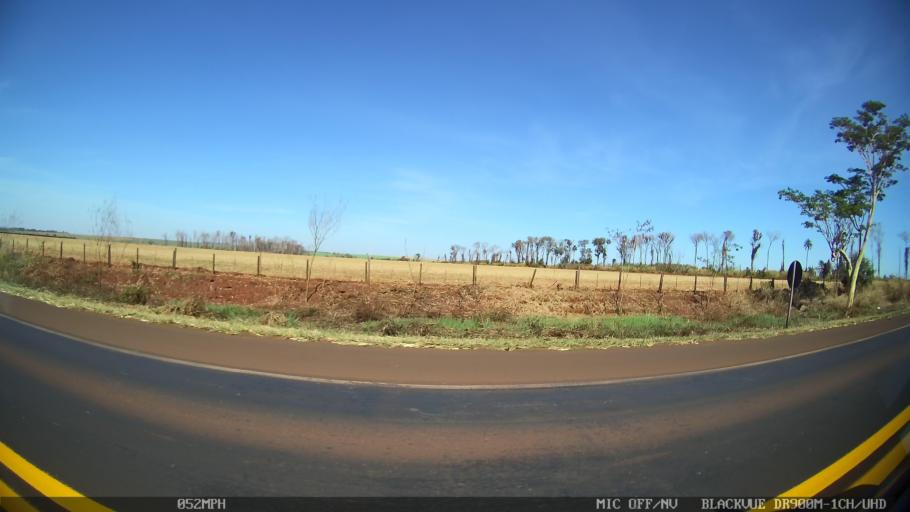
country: BR
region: Sao Paulo
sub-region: Barretos
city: Barretos
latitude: -20.4870
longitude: -48.5155
